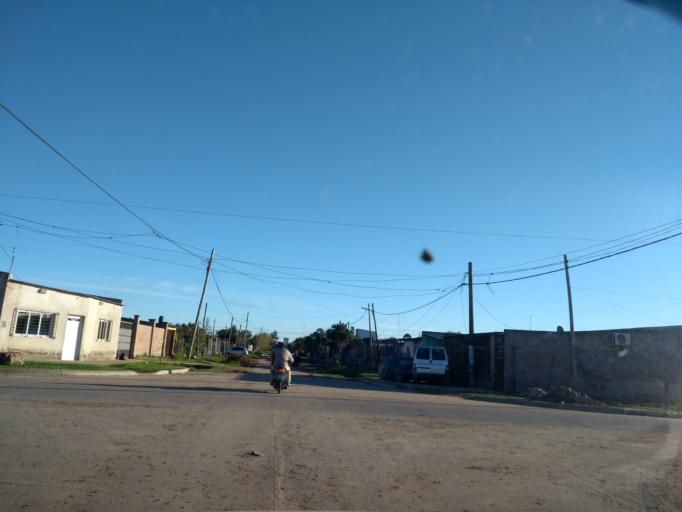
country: AR
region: Chaco
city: Barranqueras
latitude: -27.4914
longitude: -58.9369
